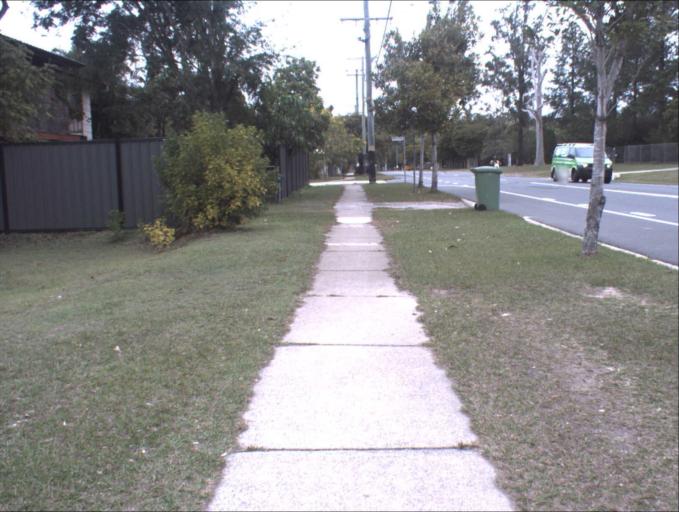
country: AU
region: Queensland
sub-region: Logan
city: Park Ridge South
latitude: -27.6885
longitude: 153.0108
